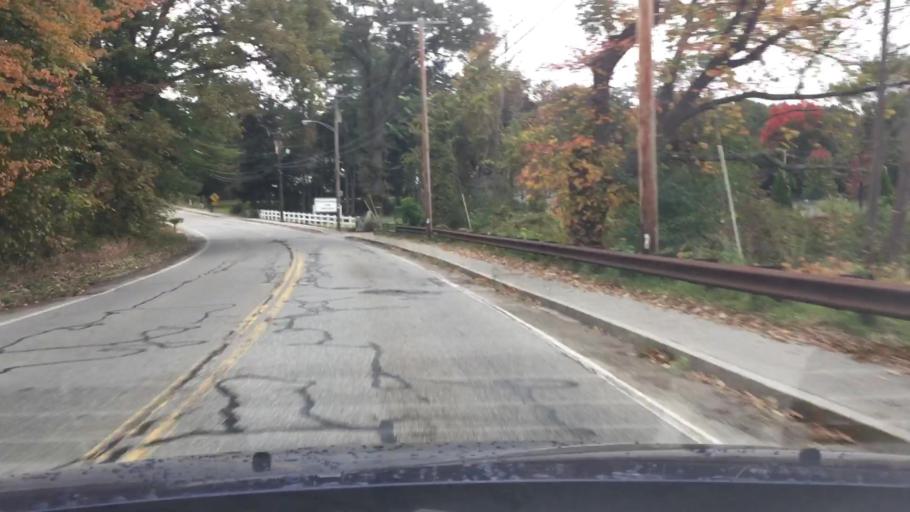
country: US
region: Massachusetts
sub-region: Middlesex County
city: Dracut
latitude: 42.6783
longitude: -71.3601
